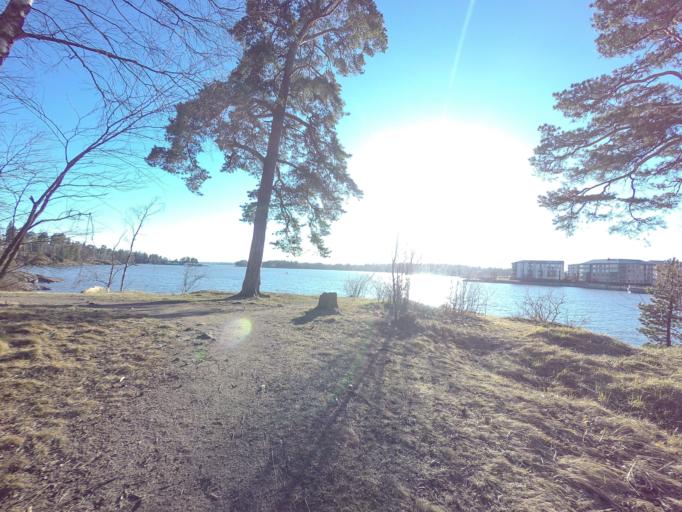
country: FI
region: Uusimaa
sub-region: Helsinki
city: Helsinki
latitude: 60.1837
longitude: 25.0352
